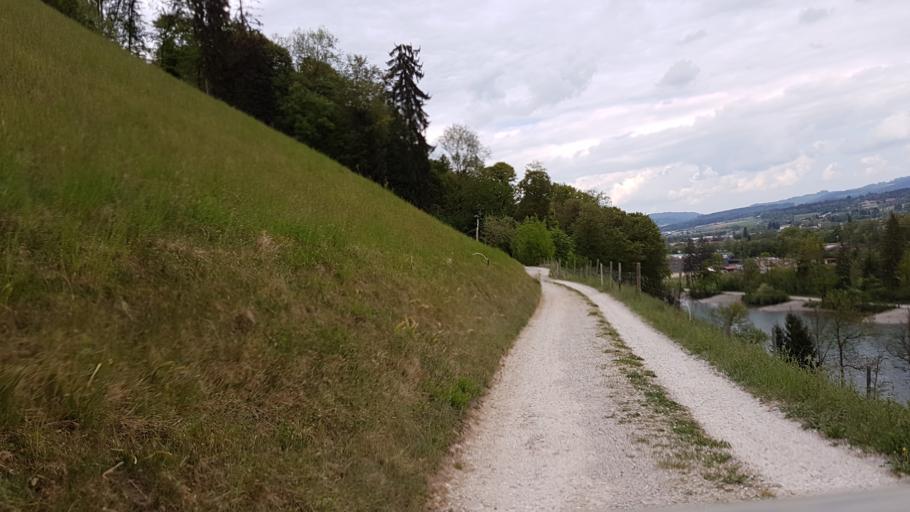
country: CH
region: Bern
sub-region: Bern-Mittelland District
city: Munsingen
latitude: 46.8607
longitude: 7.5490
